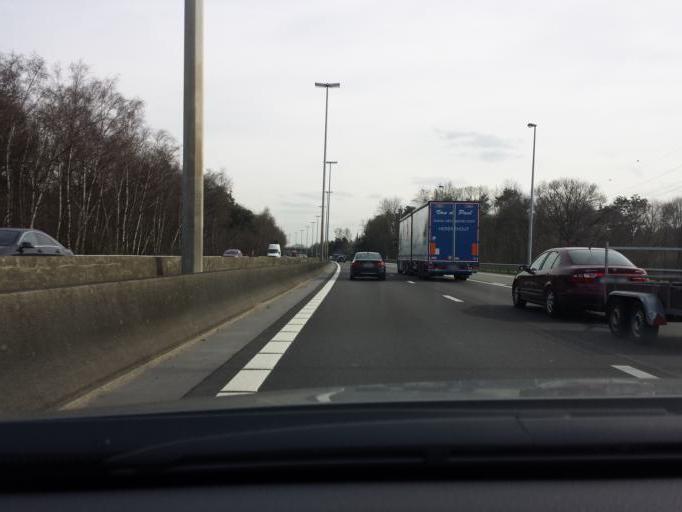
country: BE
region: Flanders
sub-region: Provincie Limburg
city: Lummen
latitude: 50.9735
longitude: 5.2433
